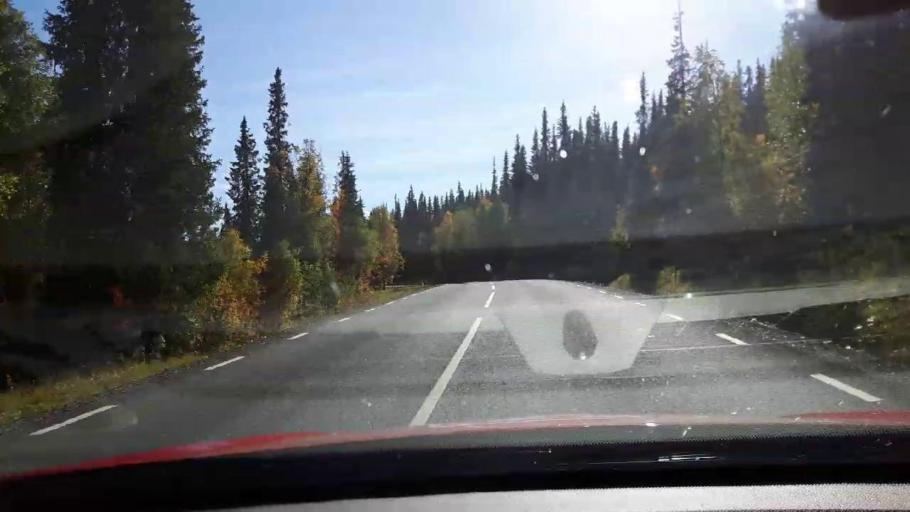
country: NO
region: Nord-Trondelag
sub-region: Royrvik
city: Royrvik
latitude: 64.8590
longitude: 14.1800
